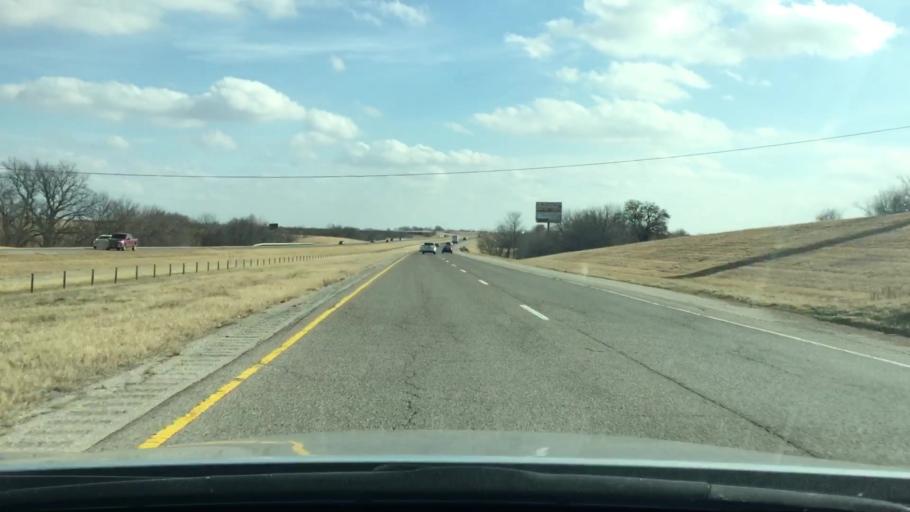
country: US
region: Oklahoma
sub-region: Garvin County
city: Maysville
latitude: 34.8960
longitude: -97.3445
